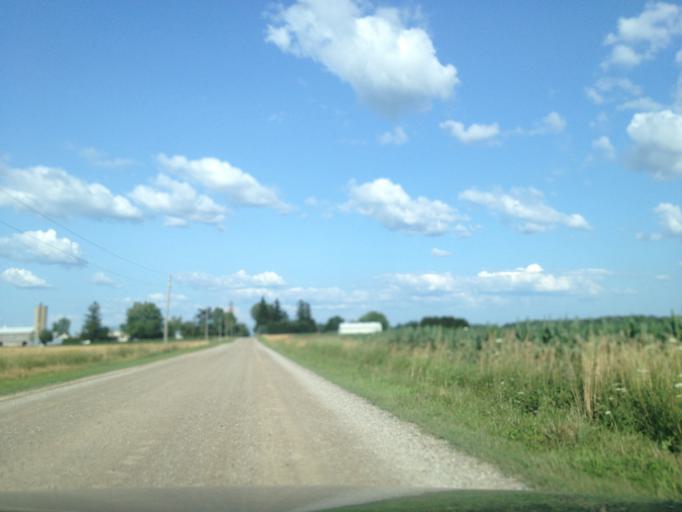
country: CA
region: Ontario
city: Ingersoll
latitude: 42.9461
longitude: -80.7728
